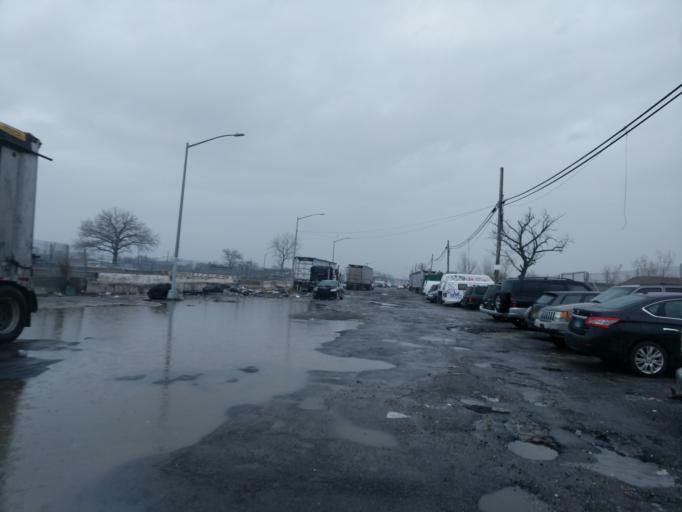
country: US
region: New York
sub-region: Queens County
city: Jamaica
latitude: 40.7560
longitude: -73.8430
